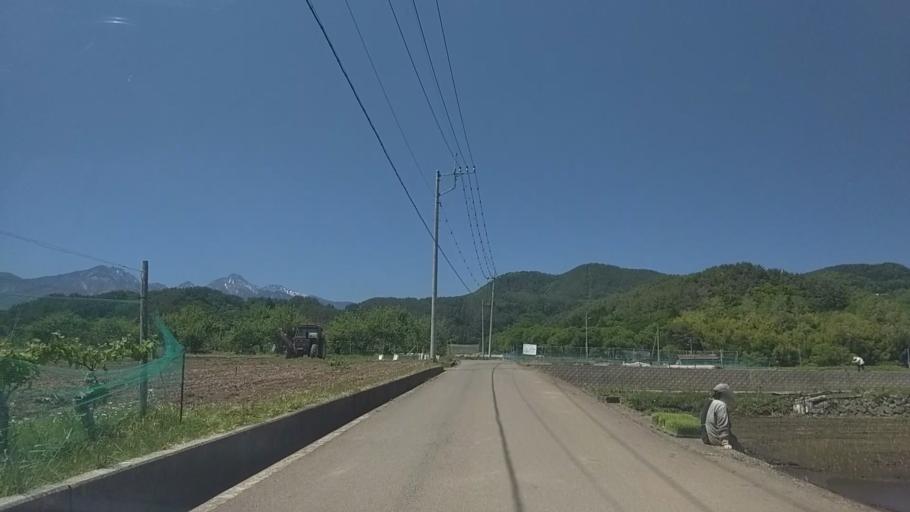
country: JP
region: Yamanashi
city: Nirasaki
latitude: 35.8526
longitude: 138.4419
